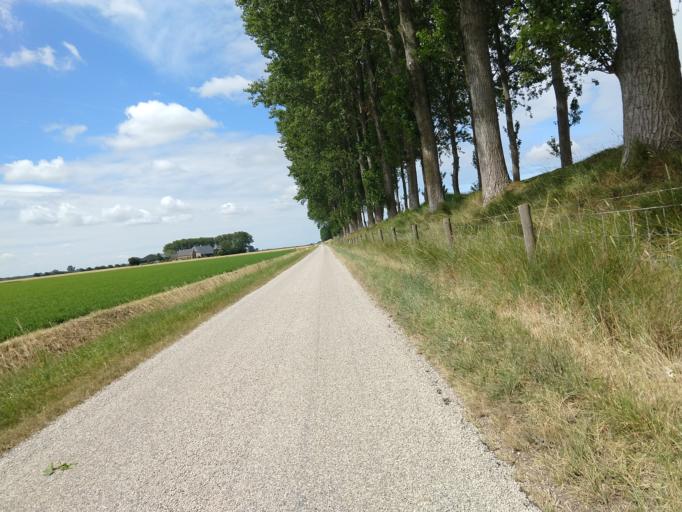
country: NL
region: Zeeland
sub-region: Gemeente Goes
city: Goes
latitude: 51.5244
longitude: 3.8017
